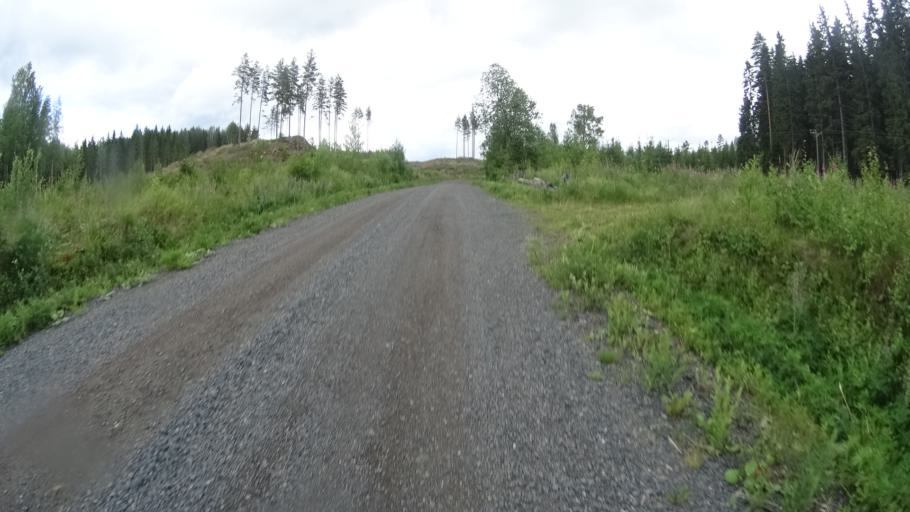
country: FI
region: Uusimaa
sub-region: Helsinki
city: Karkkila
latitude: 60.5841
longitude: 24.1685
